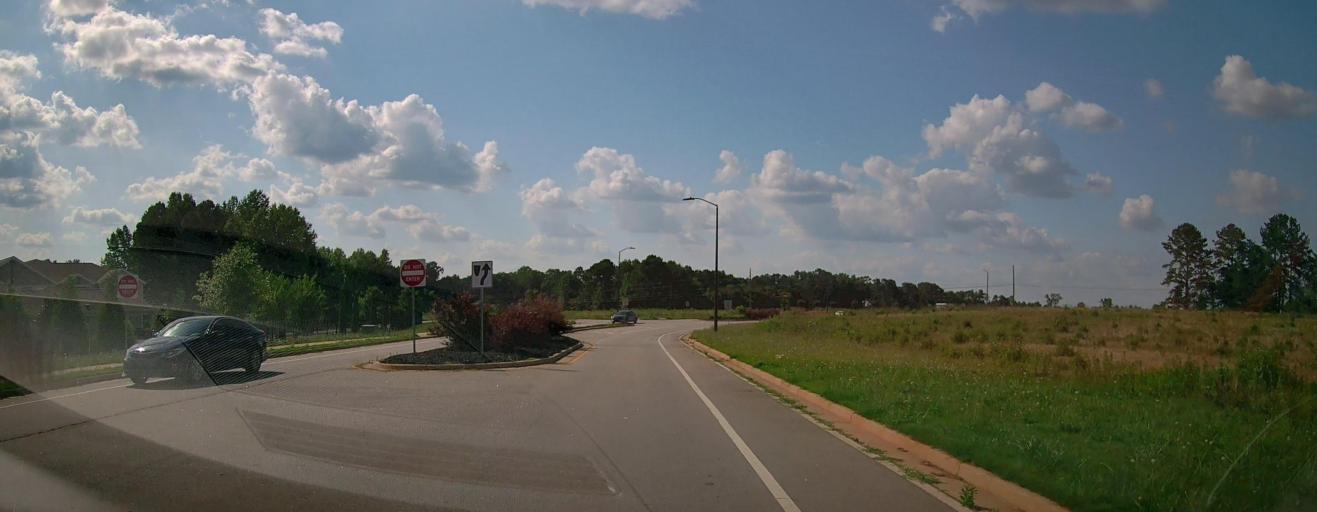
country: US
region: Georgia
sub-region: Henry County
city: McDonough
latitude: 33.4282
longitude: -84.1922
